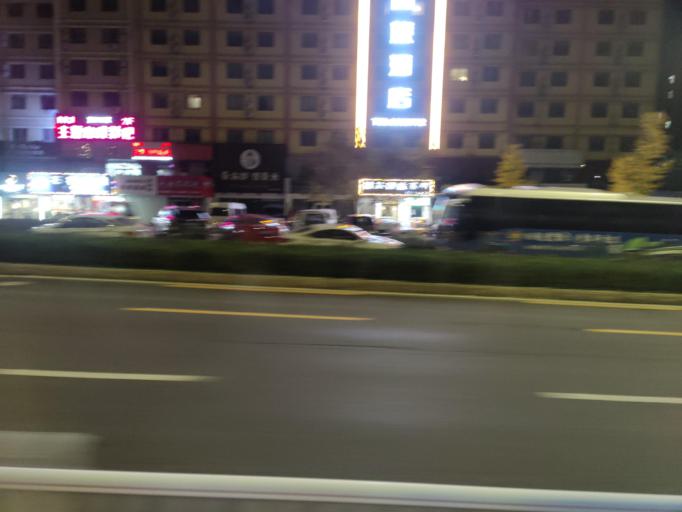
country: CN
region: Shandong Sheng
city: Shihuiyao
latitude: 37.5205
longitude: 121.3582
